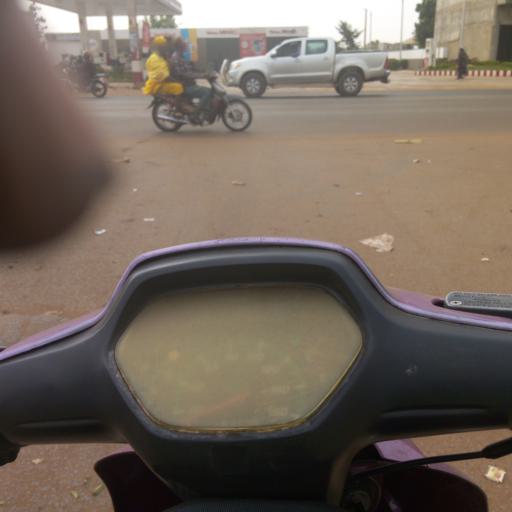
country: ML
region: Bamako
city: Bamako
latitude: 12.6639
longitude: -7.9449
